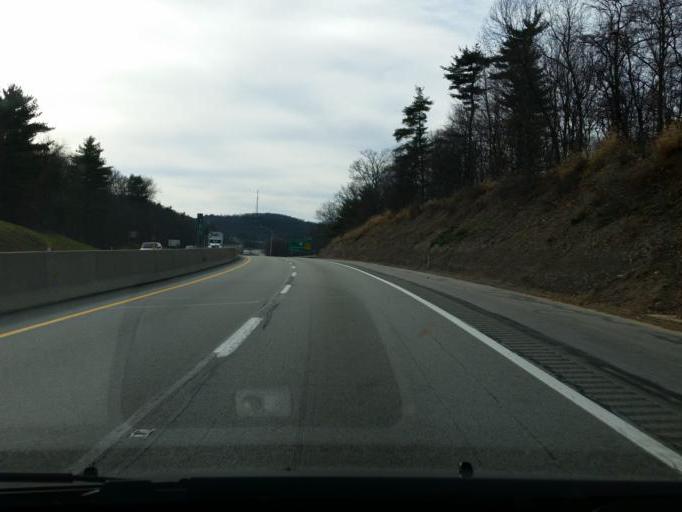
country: US
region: Pennsylvania
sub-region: Fulton County
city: McConnellsburg
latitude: 40.0578
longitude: -77.9541
